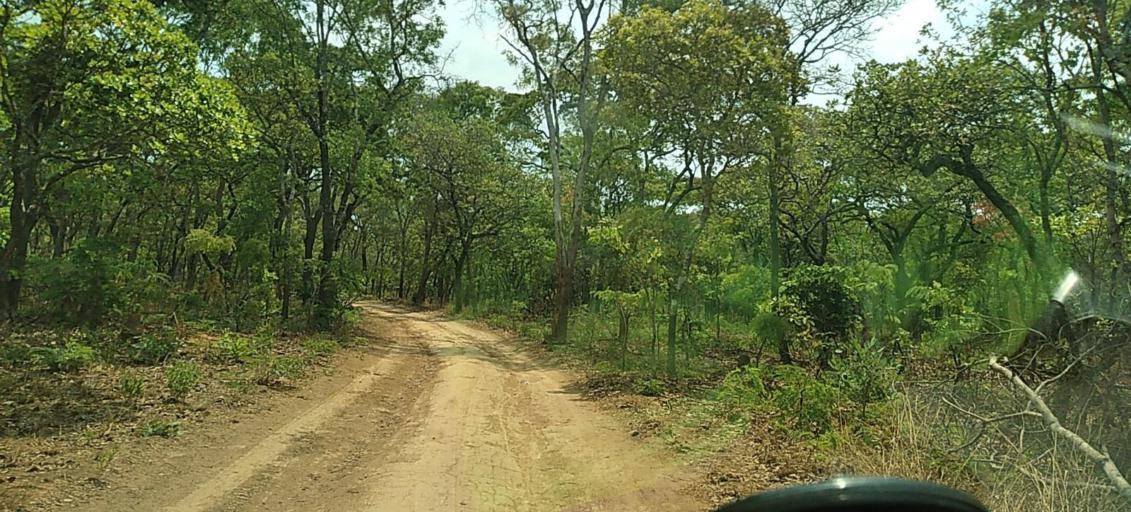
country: ZM
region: North-Western
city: Kansanshi
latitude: -12.0116
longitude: 26.2535
